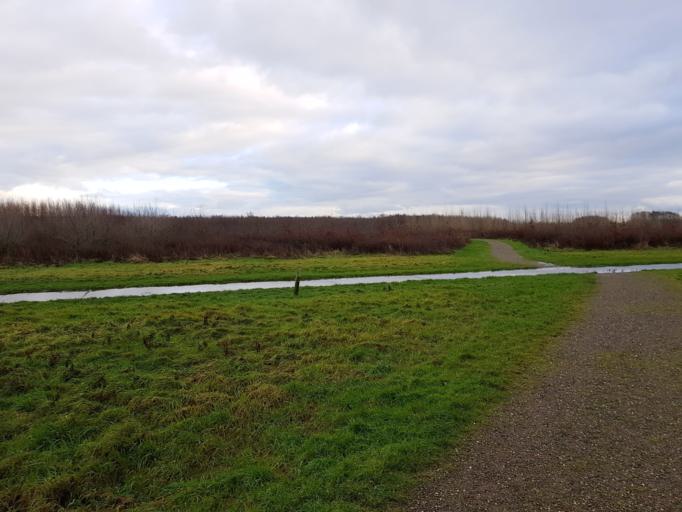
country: NL
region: South Holland
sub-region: Gemeente Rijnwoude
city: Benthuizen
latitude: 52.0710
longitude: 4.5890
